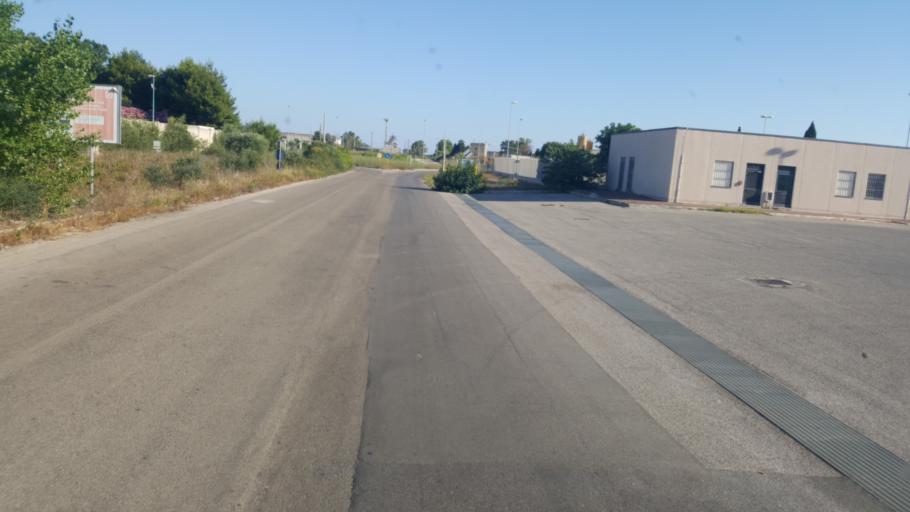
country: IT
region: Apulia
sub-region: Provincia di Brindisi
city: Materdomini
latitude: 40.6336
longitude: 17.9734
